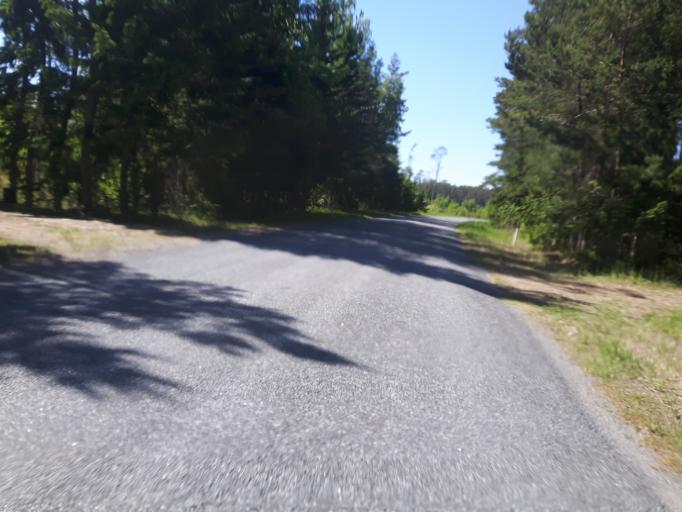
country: EE
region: Laeaene-Virumaa
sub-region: Haljala vald
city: Haljala
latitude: 59.5696
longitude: 26.2934
